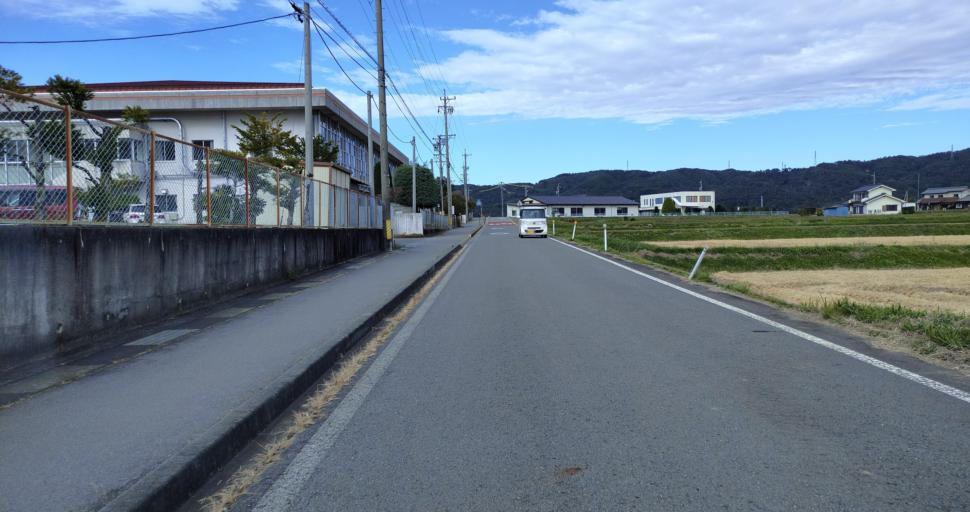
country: JP
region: Nagano
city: Komoro
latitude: 36.2687
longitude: 138.4073
